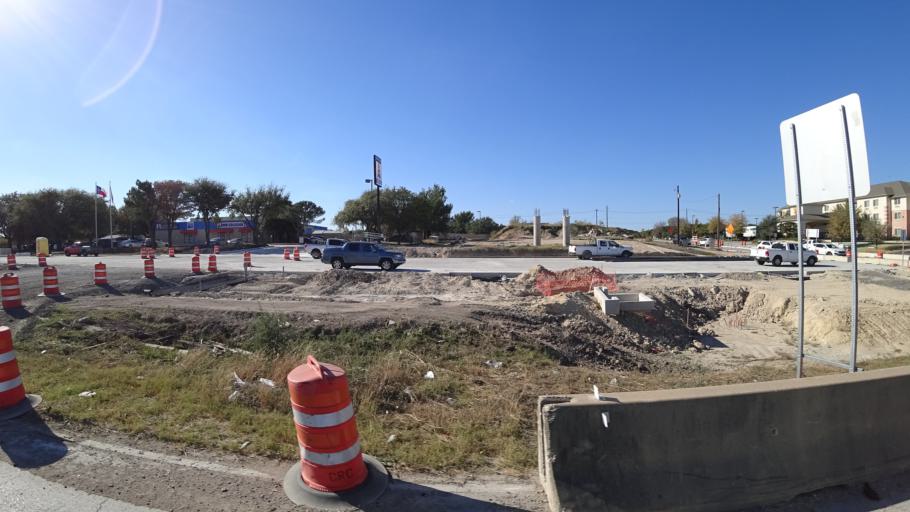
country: US
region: Texas
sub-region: Travis County
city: Austin
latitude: 30.2920
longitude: -97.6639
